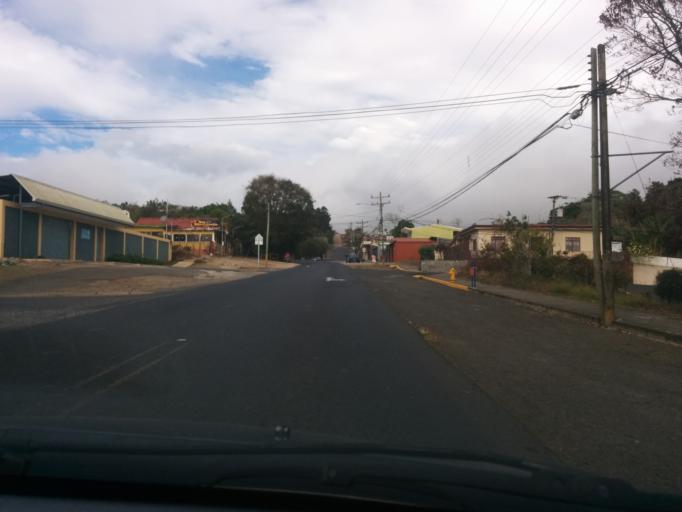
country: CR
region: Alajuela
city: San Ramon
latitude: 10.0826
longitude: -84.4725
